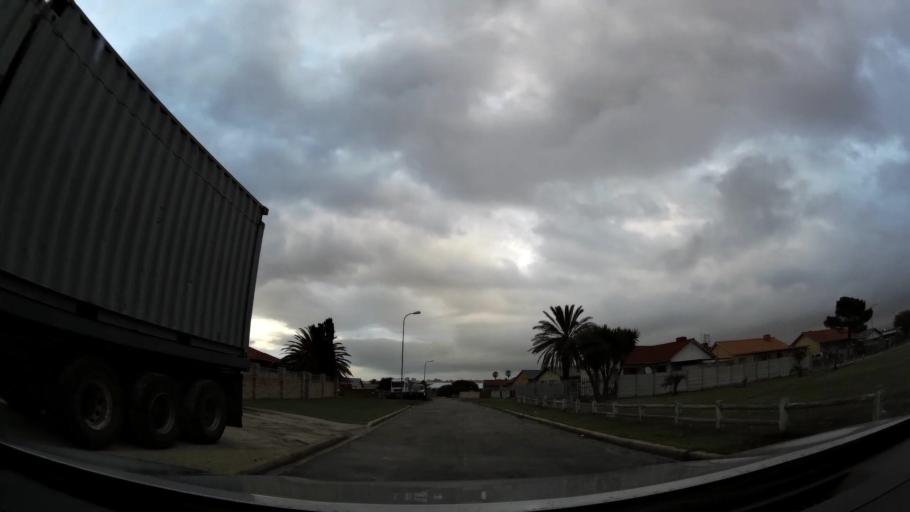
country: ZA
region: Eastern Cape
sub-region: Nelson Mandela Bay Metropolitan Municipality
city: Port Elizabeth
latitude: -33.9239
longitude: 25.6024
